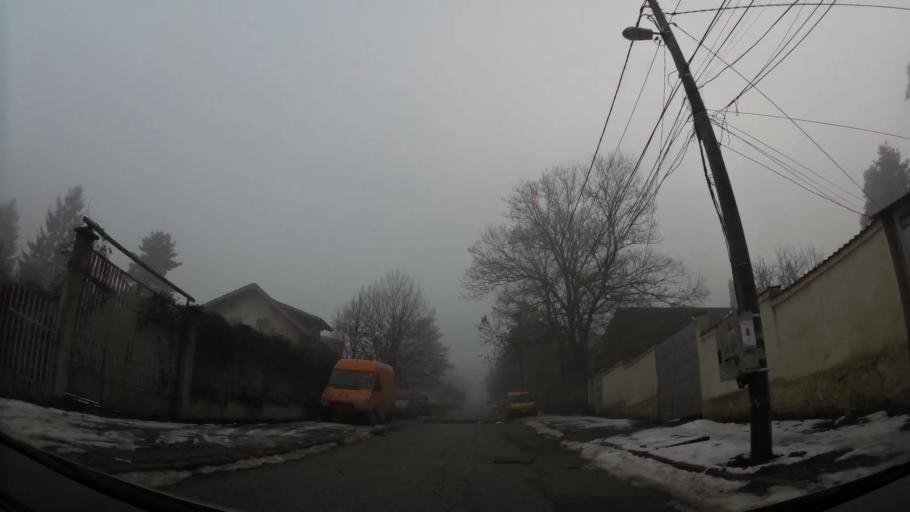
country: BG
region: Sofia-Capital
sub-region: Stolichna Obshtina
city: Sofia
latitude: 42.6597
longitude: 23.2504
